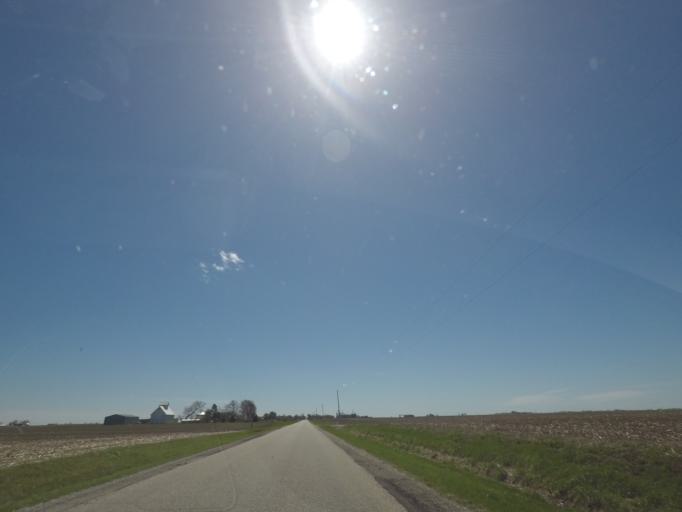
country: US
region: Illinois
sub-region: Logan County
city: Atlanta
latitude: 40.1619
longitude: -89.1936
